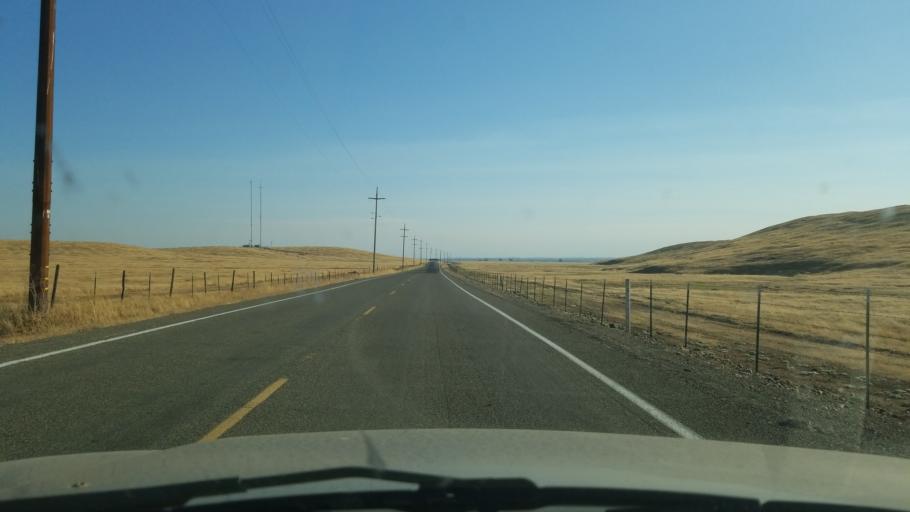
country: US
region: California
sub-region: Merced County
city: Merced
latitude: 37.4364
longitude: -120.4372
